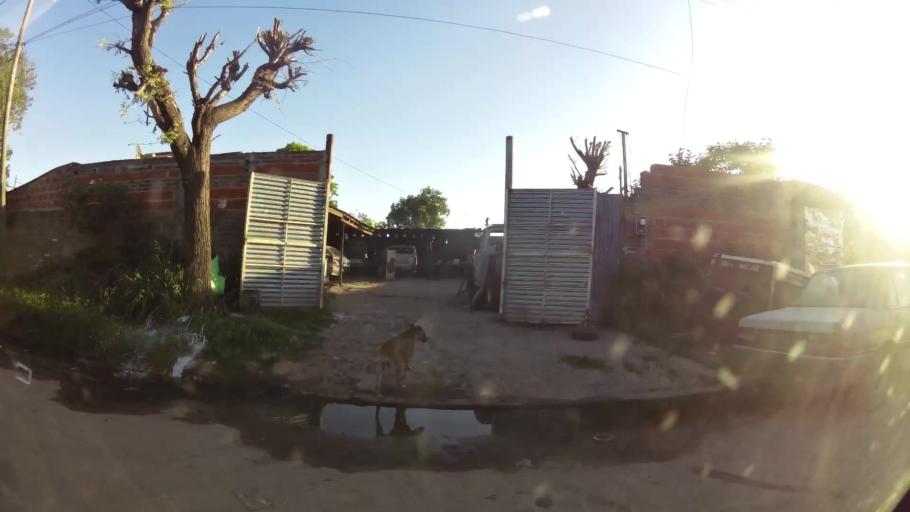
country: AR
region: Santa Fe
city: Santa Fe de la Vera Cruz
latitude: -31.5985
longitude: -60.6778
